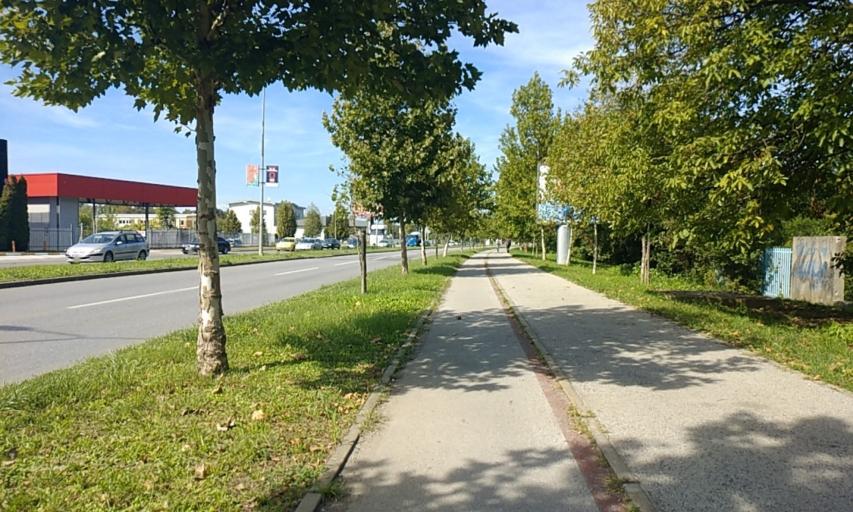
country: BA
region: Republika Srpska
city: Starcevica
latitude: 44.7760
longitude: 17.2073
